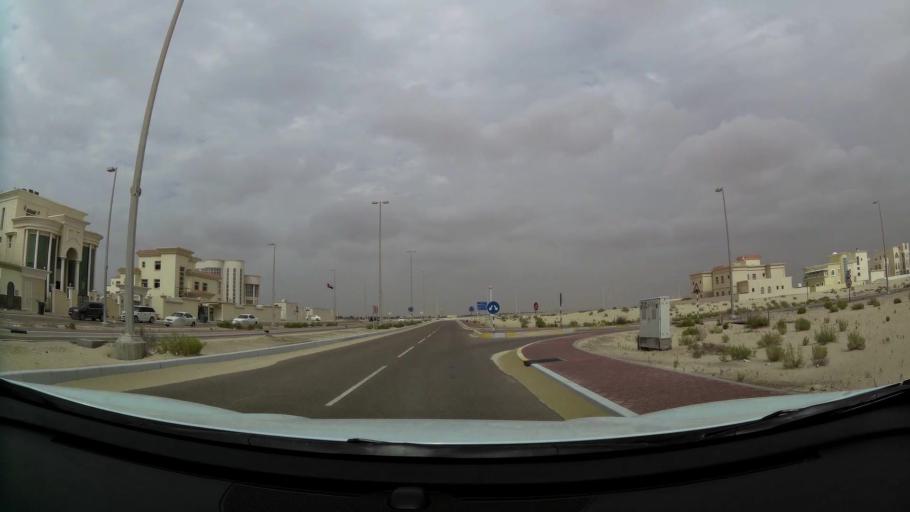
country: AE
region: Abu Dhabi
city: Abu Dhabi
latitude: 24.3982
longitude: 54.6558
